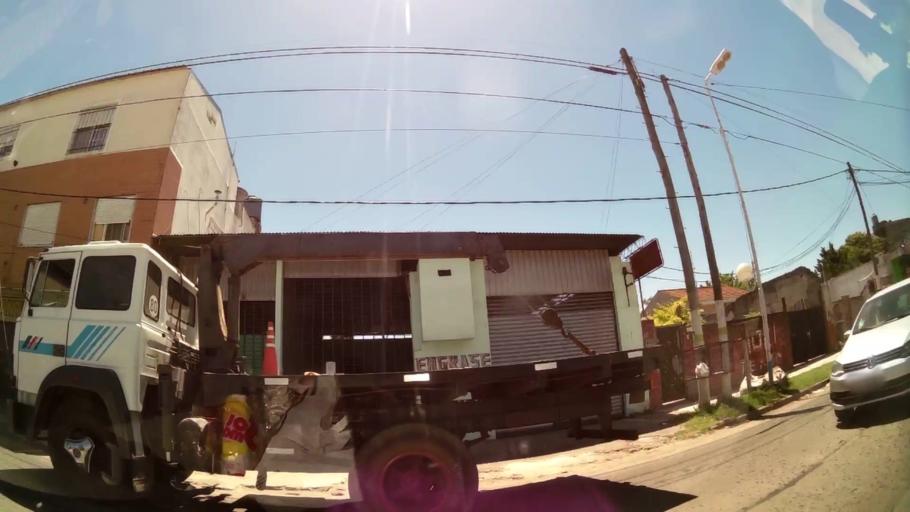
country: AR
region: Buenos Aires
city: Hurlingham
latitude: -34.5026
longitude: -58.6819
